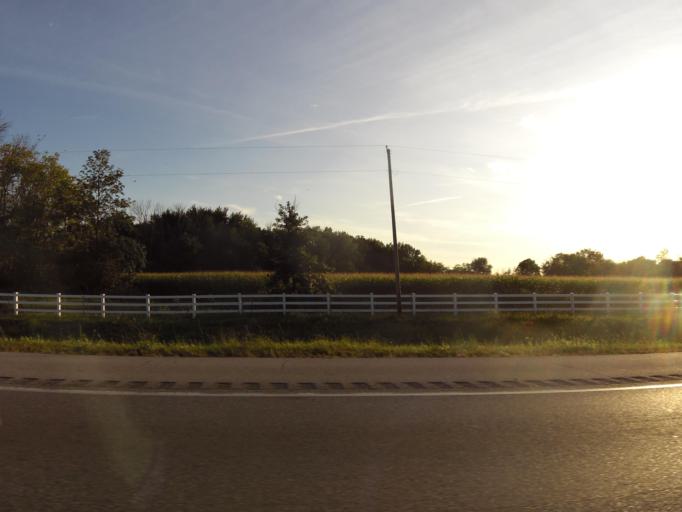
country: US
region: Indiana
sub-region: Boone County
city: Whitestown
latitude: 39.9582
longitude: -86.3675
